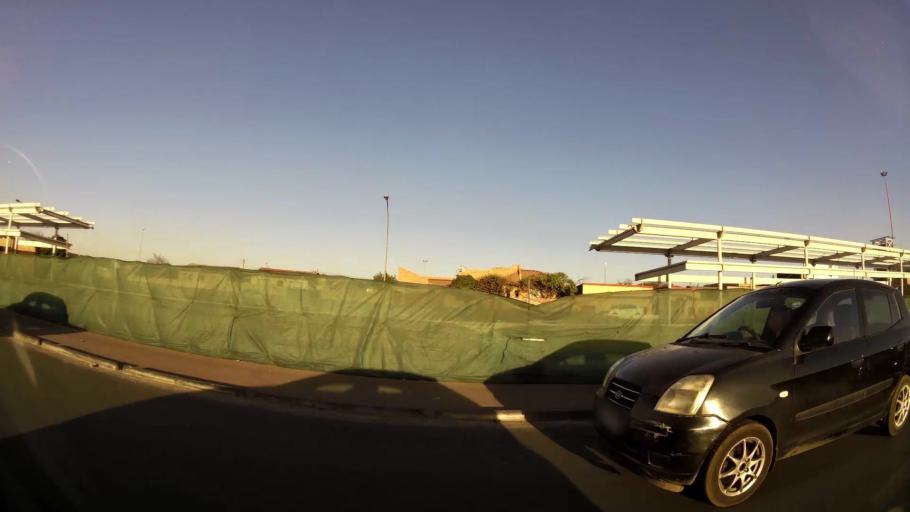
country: ZA
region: Gauteng
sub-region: Ekurhuleni Metropolitan Municipality
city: Tembisa
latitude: -26.0197
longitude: 28.2003
